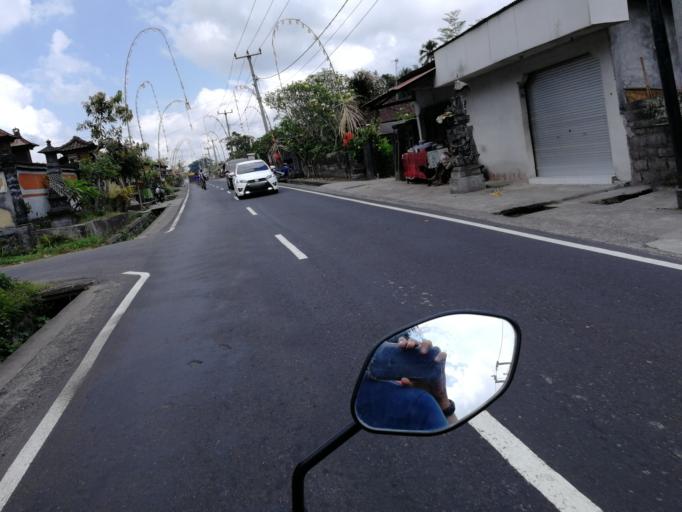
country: ID
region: Bali
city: Banjar Geriana Kangin
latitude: -8.4281
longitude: 115.4358
